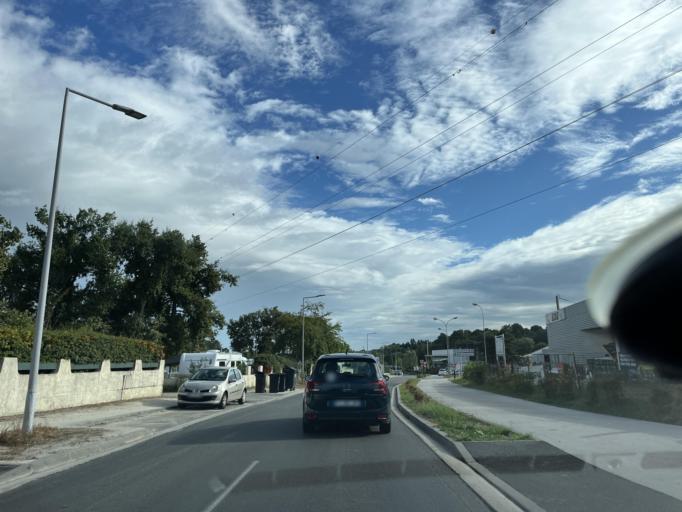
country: FR
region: Aquitaine
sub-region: Departement de la Gironde
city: Le Haillan
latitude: 44.8692
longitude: -0.6629
